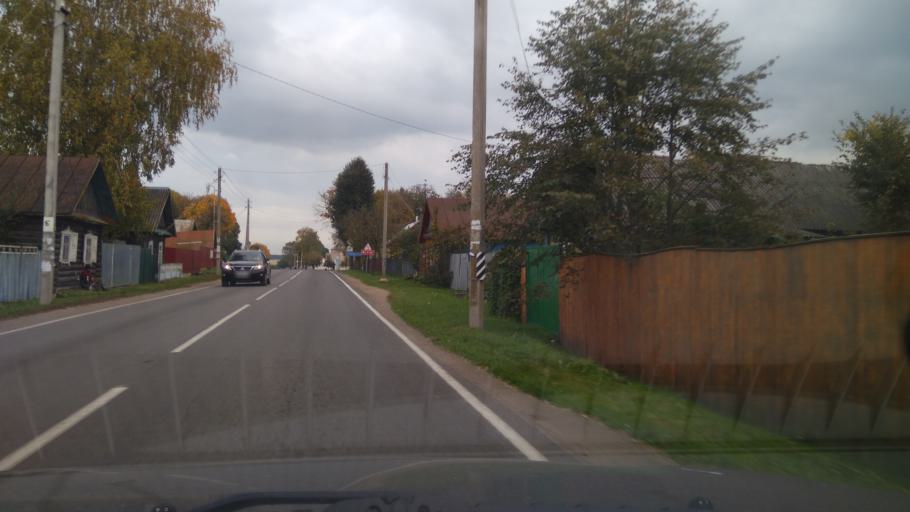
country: BY
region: Minsk
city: Dukora
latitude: 53.6689
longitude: 27.9501
